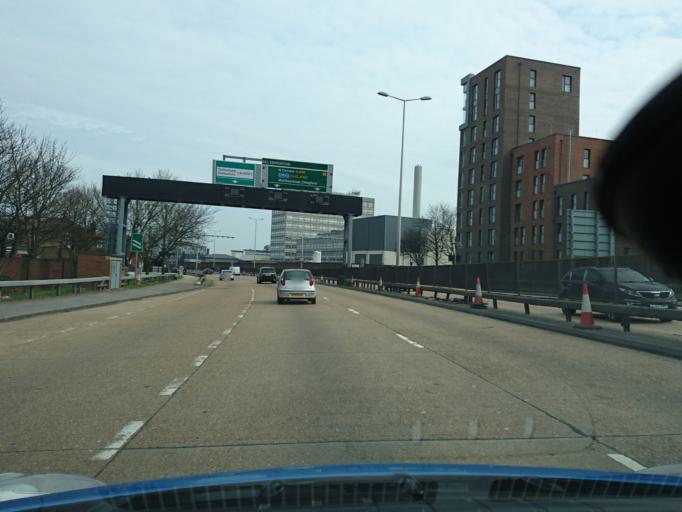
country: GB
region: England
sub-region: Greater London
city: Enfield
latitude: 51.6144
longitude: -0.0777
